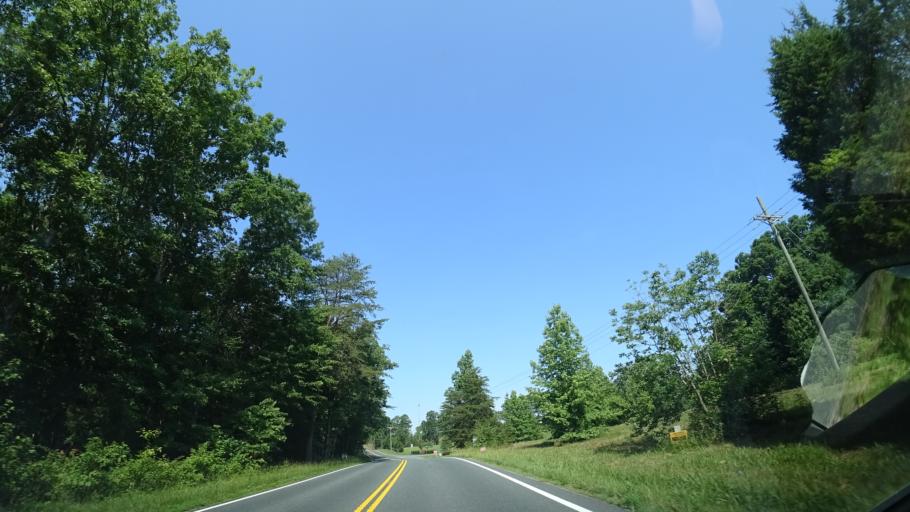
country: US
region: Virginia
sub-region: Louisa County
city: Louisa
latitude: 38.0841
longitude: -77.8427
